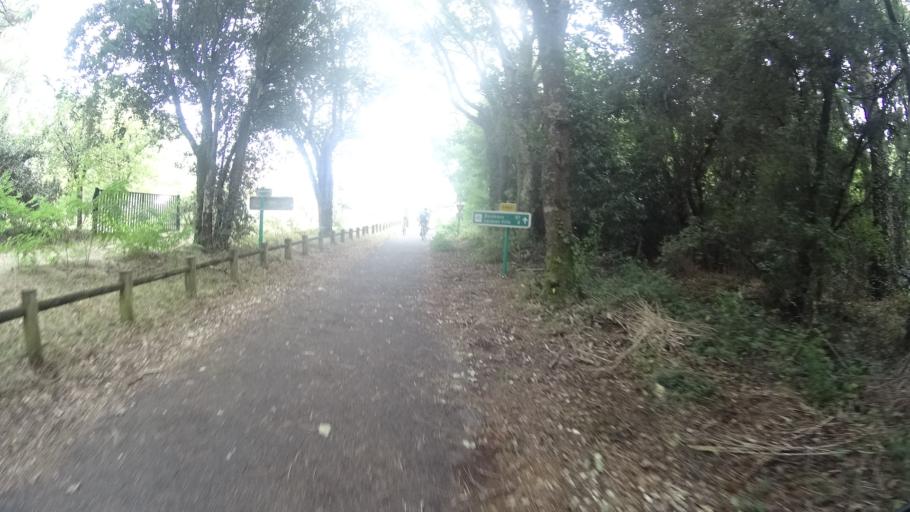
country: FR
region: Aquitaine
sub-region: Departement de la Gironde
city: Lacanau
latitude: 45.0038
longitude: -1.1375
